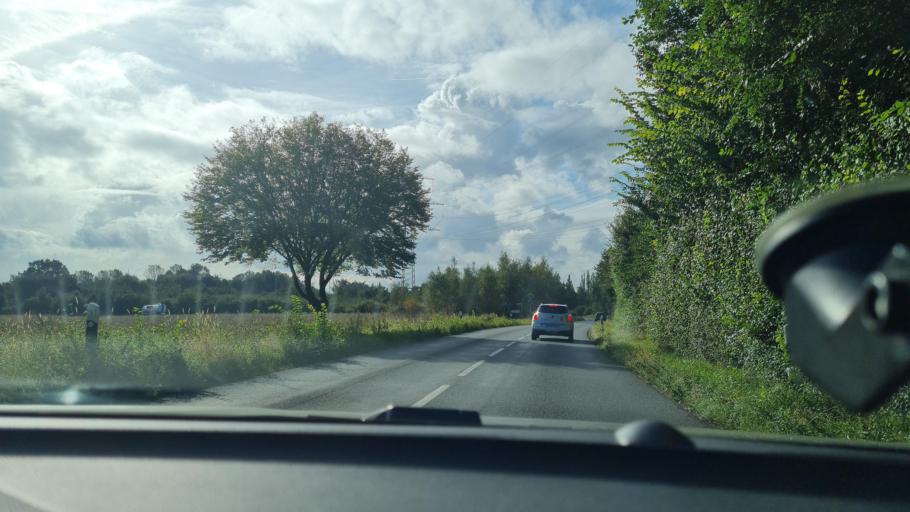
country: DE
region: North Rhine-Westphalia
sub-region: Regierungsbezirk Dusseldorf
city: Dinslaken
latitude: 51.5396
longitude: 6.7707
